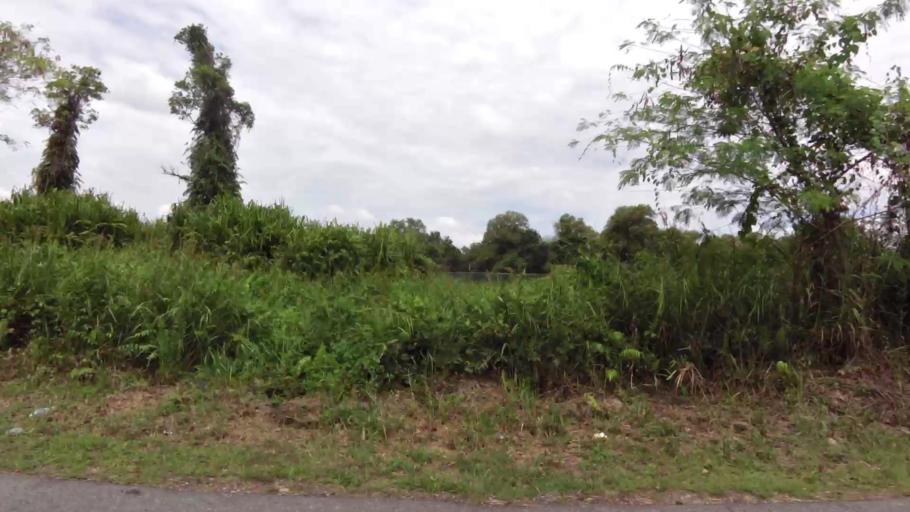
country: BN
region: Brunei and Muara
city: Bandar Seri Begawan
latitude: 4.9229
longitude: 114.9150
